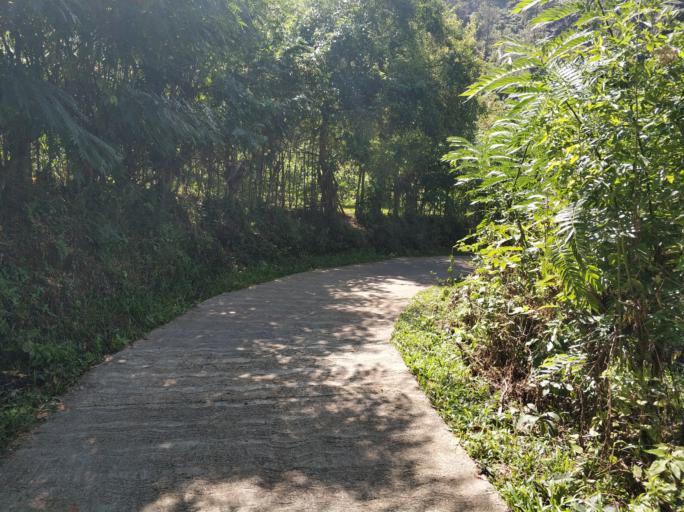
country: LK
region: Uva
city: Haputale
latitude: 6.8316
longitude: 81.0553
